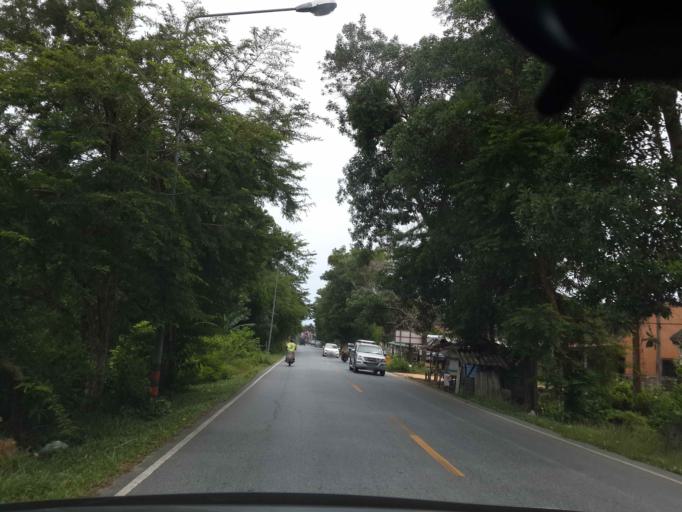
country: TH
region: Narathiwat
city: Yi-ngo
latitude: 6.4007
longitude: 101.7012
